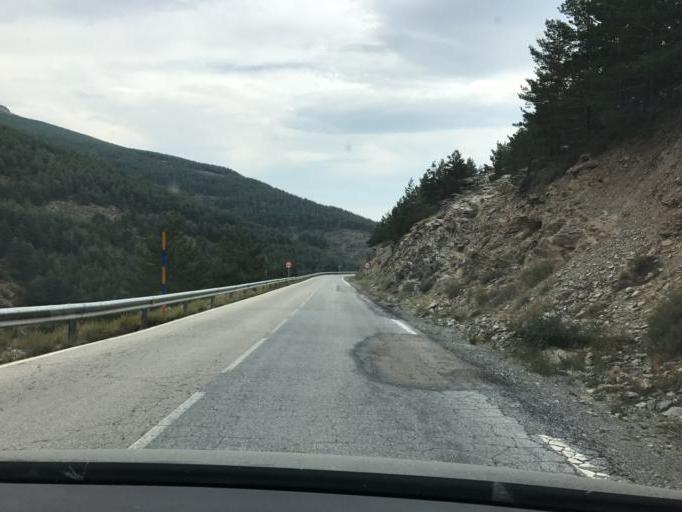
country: ES
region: Andalusia
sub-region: Provincia de Almeria
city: Bayarcal
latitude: 37.0958
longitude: -3.0237
